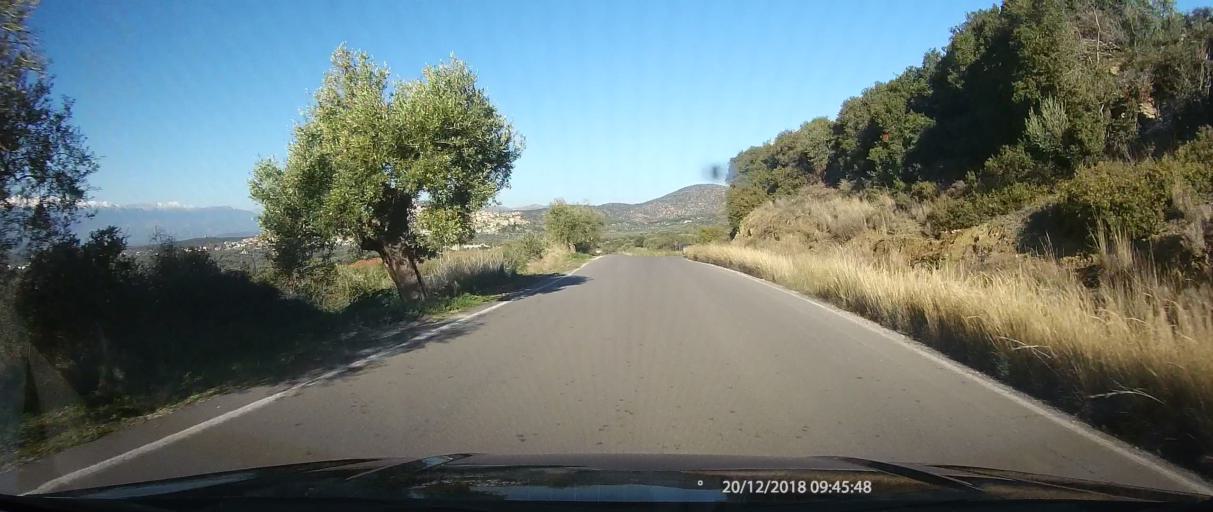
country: GR
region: Peloponnese
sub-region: Nomos Lakonias
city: Yerakion
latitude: 36.9868
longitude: 22.7221
